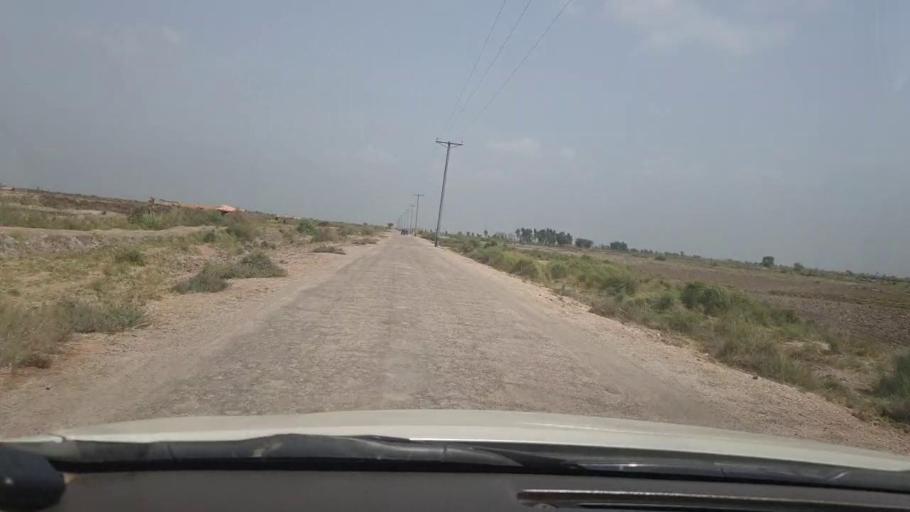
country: PK
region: Sindh
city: Garhi Yasin
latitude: 27.9972
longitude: 68.5008
